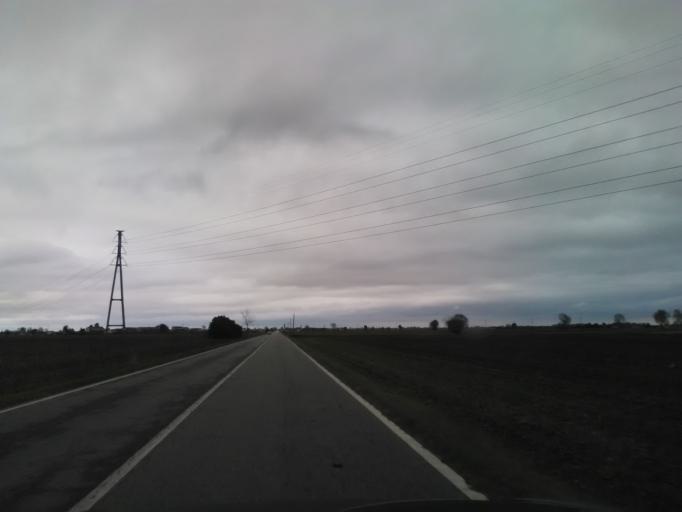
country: IT
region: Piedmont
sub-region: Provincia di Vercelli
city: Bianze
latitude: 45.3320
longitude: 8.1225
